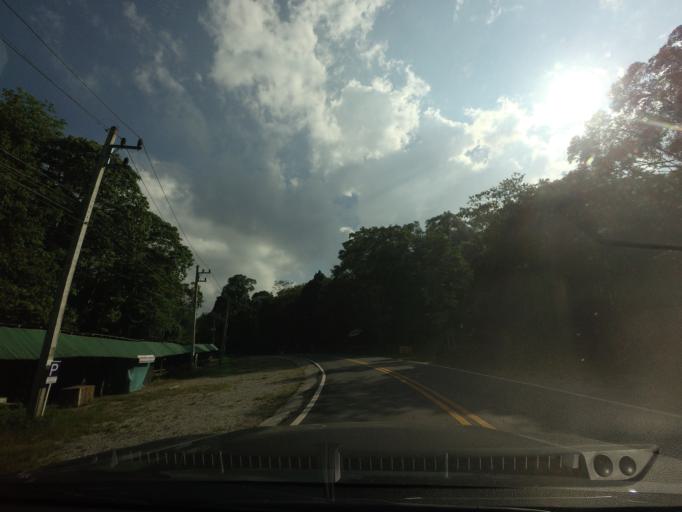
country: TH
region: Phitsanulok
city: Nakhon Thai
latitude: 16.9937
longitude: 101.0124
